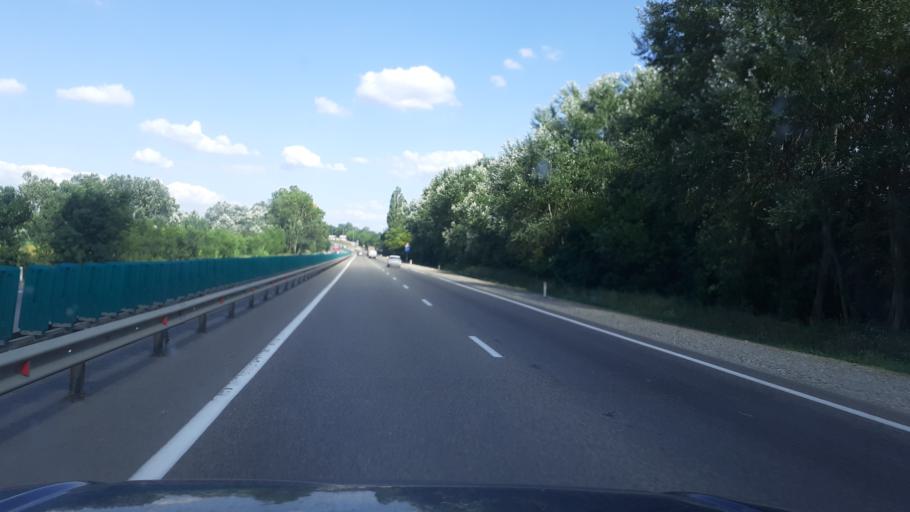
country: RU
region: Krasnodarskiy
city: Severskaya
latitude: 44.8544
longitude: 38.7341
